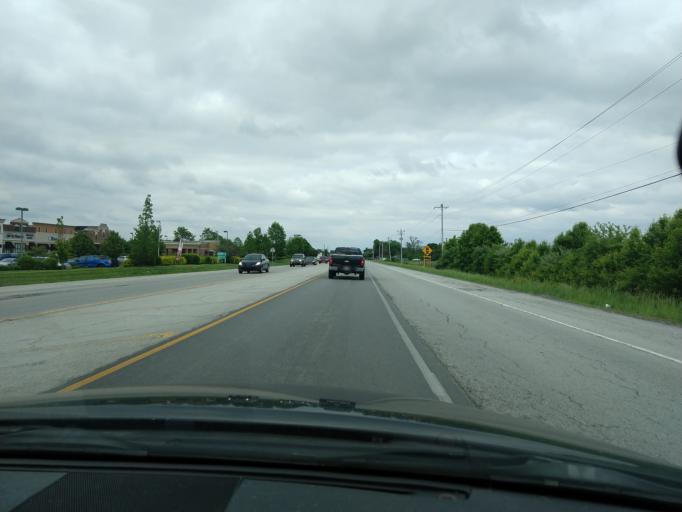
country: US
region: Indiana
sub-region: Hamilton County
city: Westfield
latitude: 40.0431
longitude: -86.0752
